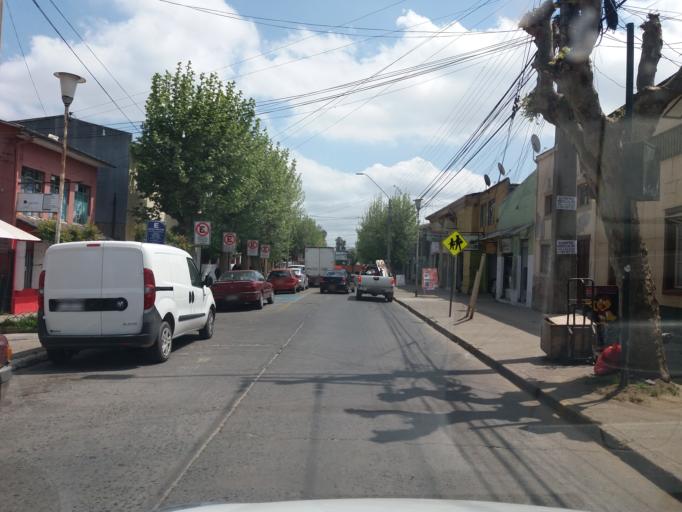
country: CL
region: Valparaiso
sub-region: Provincia de Marga Marga
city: Limache
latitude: -32.9839
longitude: -71.2750
